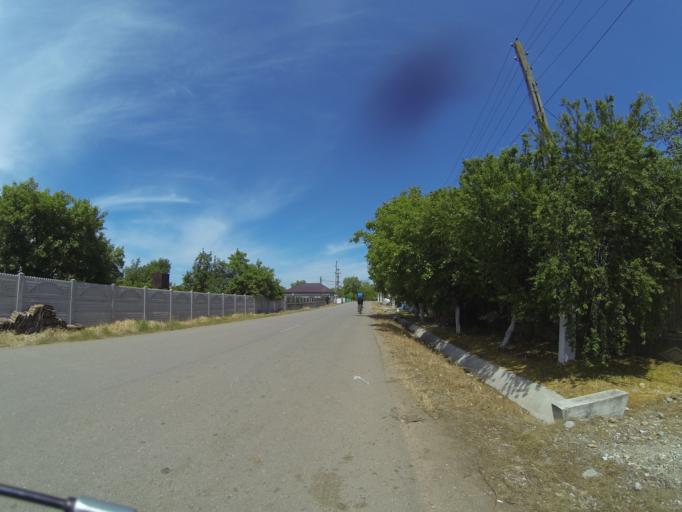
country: RO
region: Dolj
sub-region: Comuna Diosti
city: Radomir
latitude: 44.1591
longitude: 24.1626
